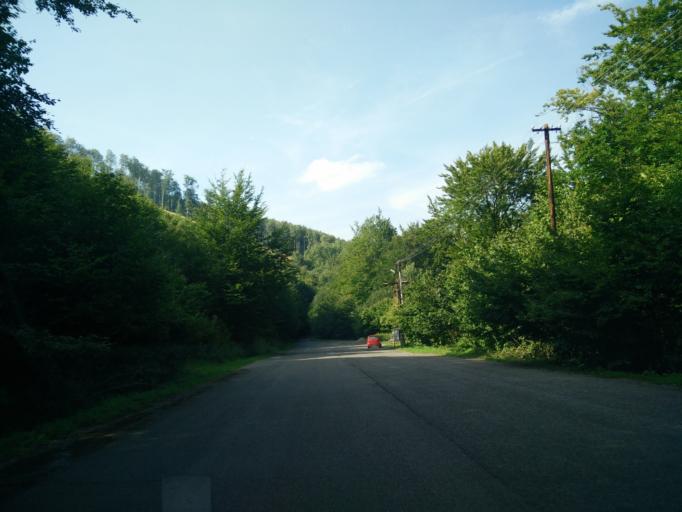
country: SK
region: Nitriansky
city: Novaky
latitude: 48.6651
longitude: 18.6282
